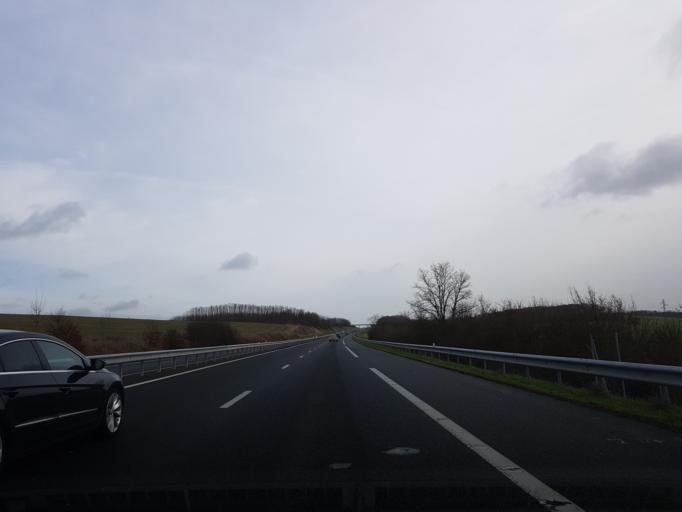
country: FR
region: Bourgogne
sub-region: Departement de l'Yonne
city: Thorigny-sur-Oreuse
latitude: 48.2354
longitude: 3.4057
